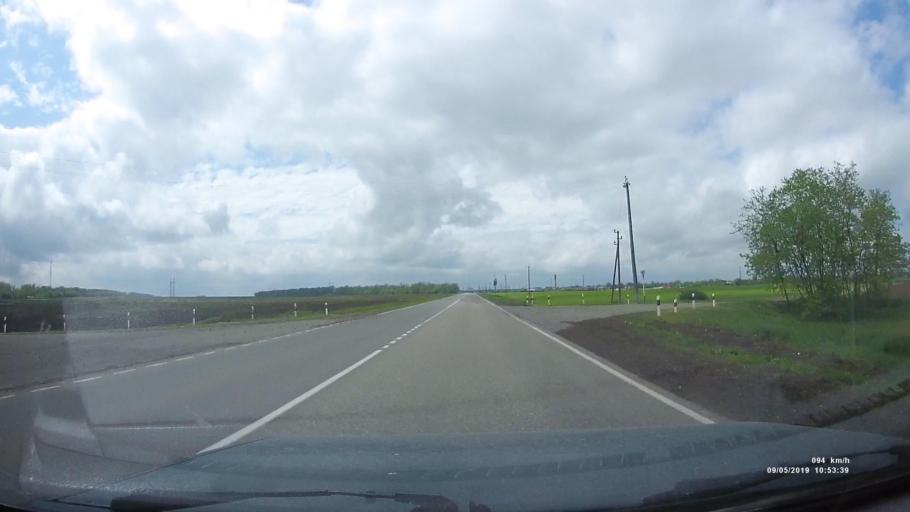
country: RU
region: Rostov
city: Peshkovo
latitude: 46.8845
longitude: 39.3372
